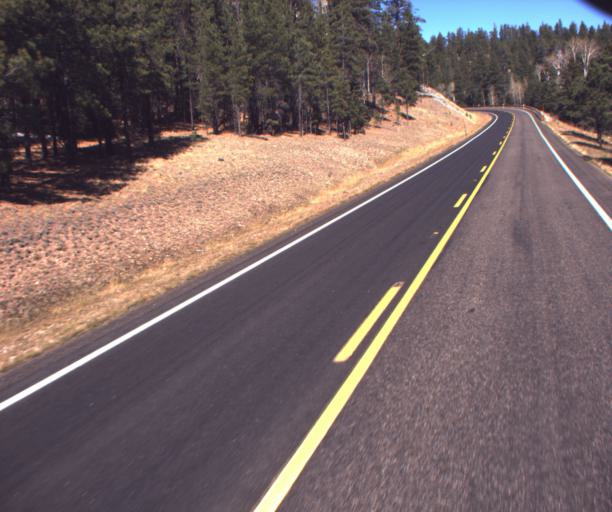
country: US
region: Arizona
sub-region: Coconino County
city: Grand Canyon
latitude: 36.5092
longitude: -112.1382
